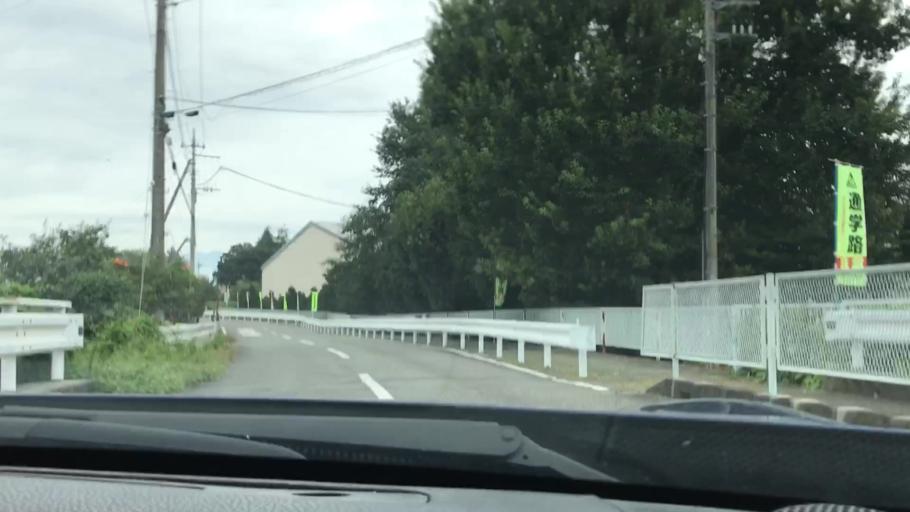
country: JP
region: Gunma
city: Kanekomachi
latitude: 36.4016
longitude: 138.9929
